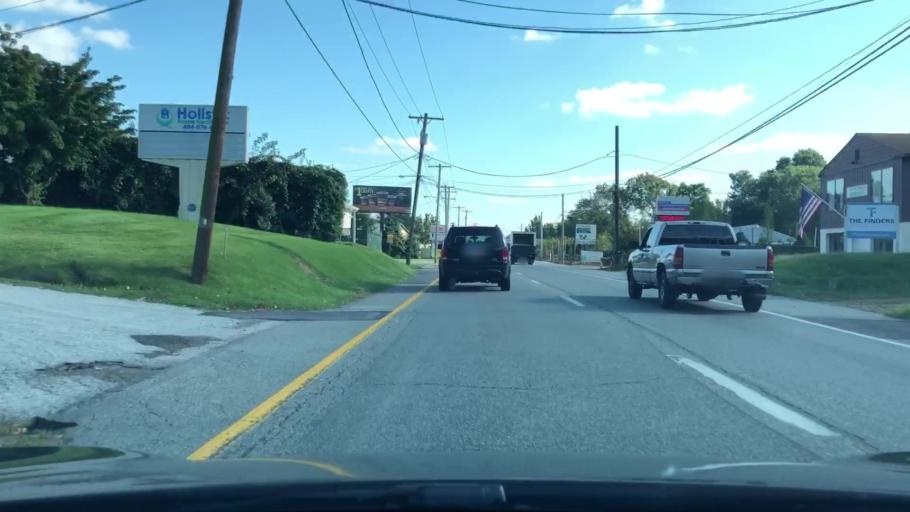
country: US
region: Pennsylvania
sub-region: Delaware County
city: Chester Heights
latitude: 39.8532
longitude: -75.5402
